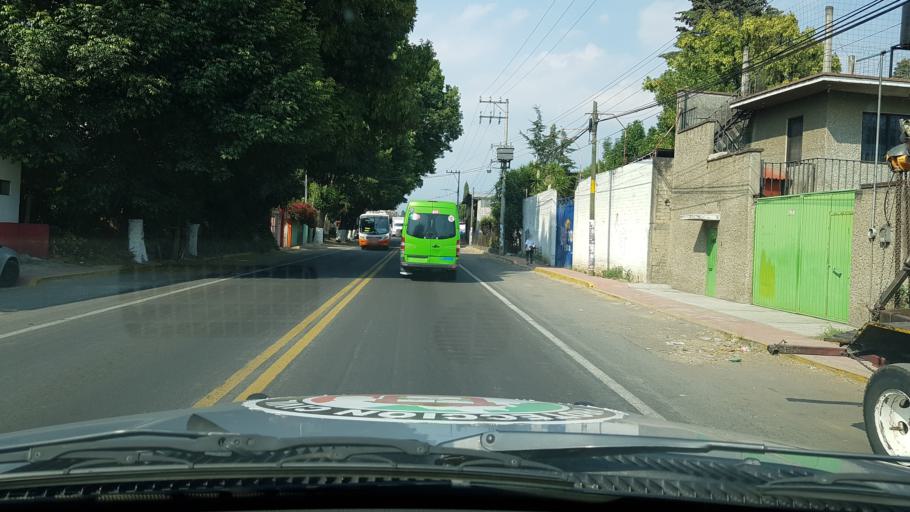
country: MX
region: Mexico
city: Tepetlixpa
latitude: 19.0284
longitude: -98.8151
